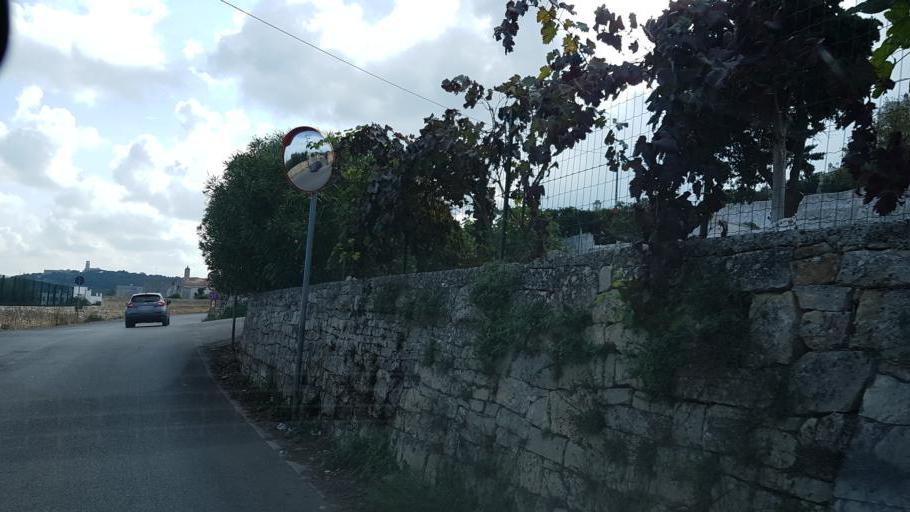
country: IT
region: Apulia
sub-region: Provincia di Brindisi
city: Ostuni
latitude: 40.7356
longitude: 17.5804
